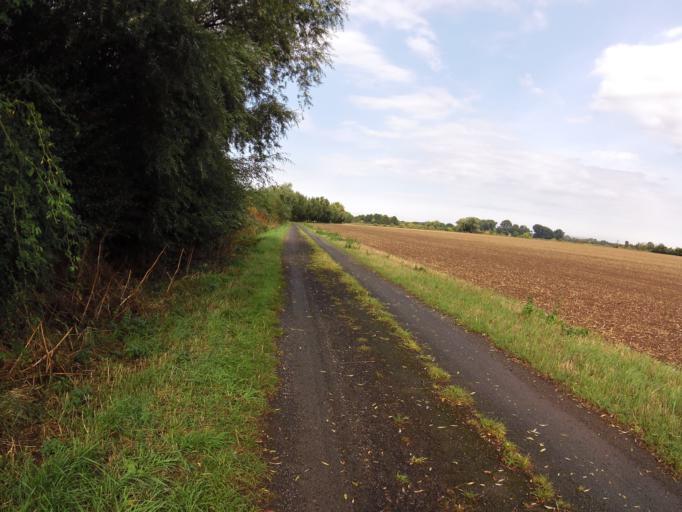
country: DE
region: Lower Saxony
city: Marklohe
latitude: 52.6582
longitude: 9.1893
